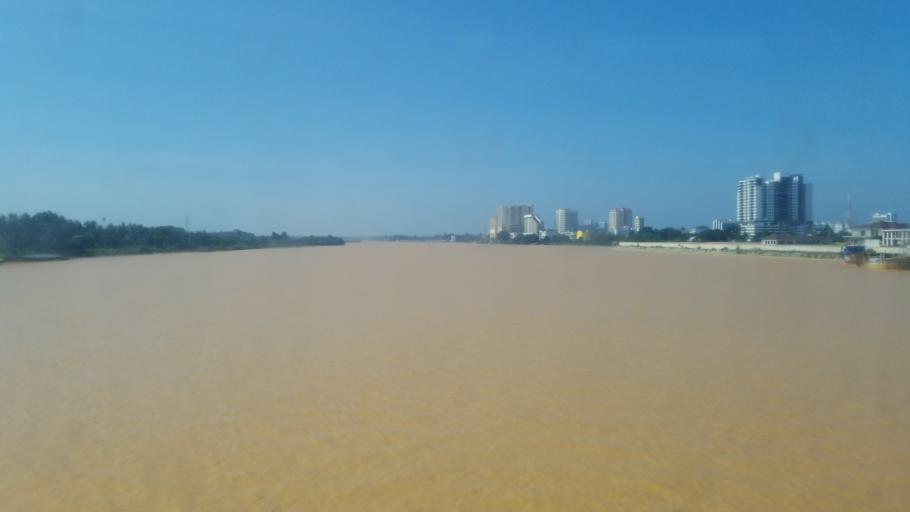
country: MY
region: Kelantan
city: Kota Bharu
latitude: 6.1165
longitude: 102.2289
